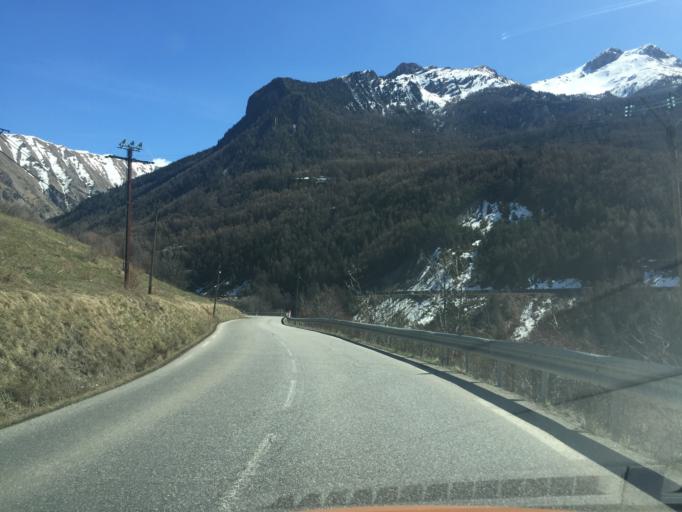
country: FR
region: Provence-Alpes-Cote d'Azur
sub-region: Departement des Hautes-Alpes
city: Embrun
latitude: 44.5129
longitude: 6.5610
